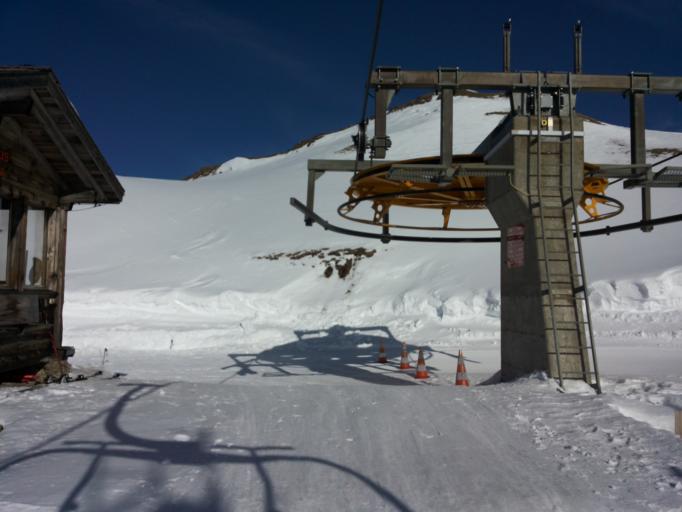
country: CH
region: Bern
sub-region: Interlaken-Oberhasli District
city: Meiringen
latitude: 46.7633
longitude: 8.2588
